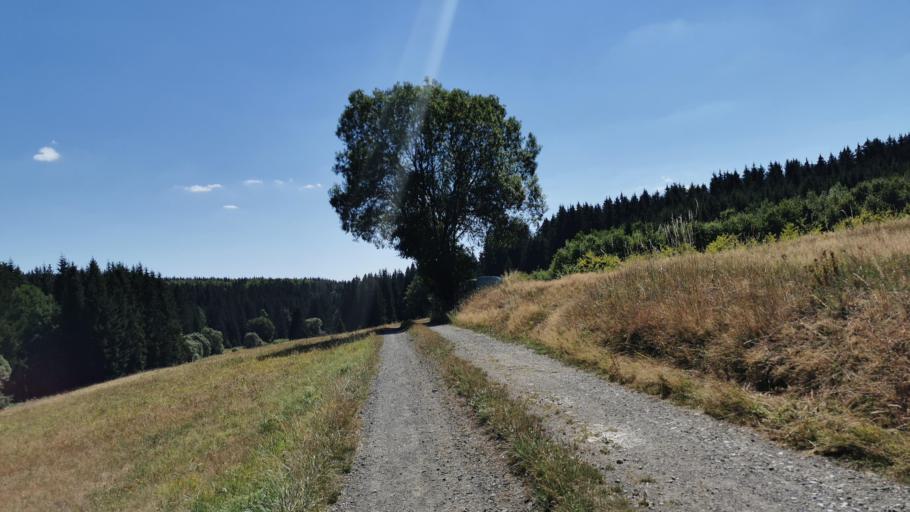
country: DE
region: Bavaria
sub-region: Upper Franconia
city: Pressig
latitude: 50.4147
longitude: 11.2928
